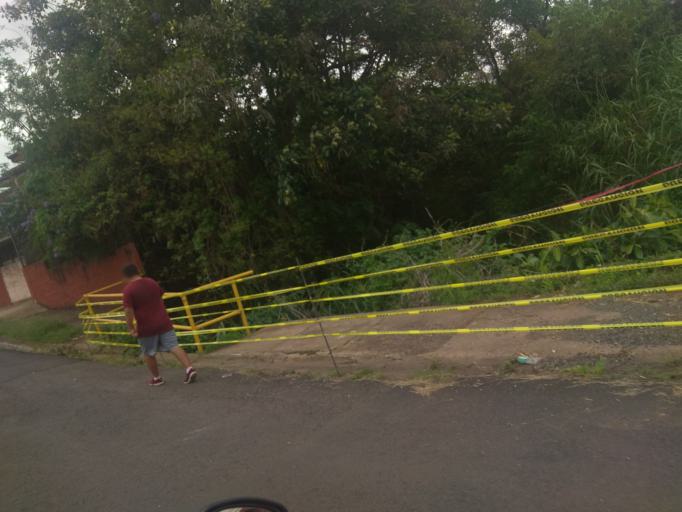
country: CR
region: Heredia
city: San Rafael
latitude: 10.0083
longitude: -84.1017
